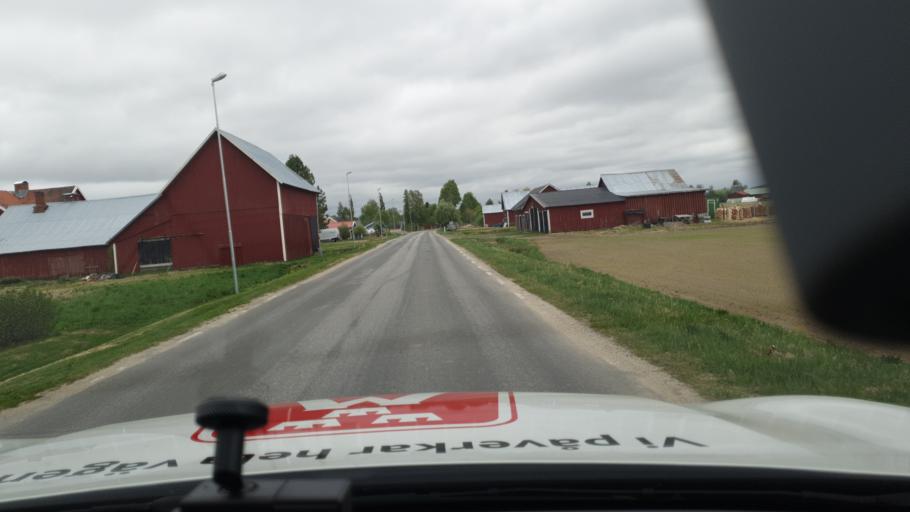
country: SE
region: Vaesterbotten
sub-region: Vannas Kommun
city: Vannasby
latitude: 63.9463
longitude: 19.8644
